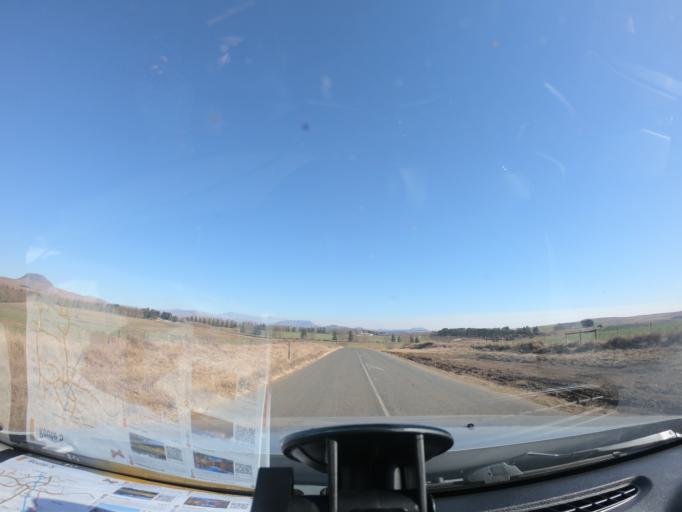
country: ZA
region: KwaZulu-Natal
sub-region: uMgungundlovu District Municipality
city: Mooirivier
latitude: -29.3249
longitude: 29.8361
